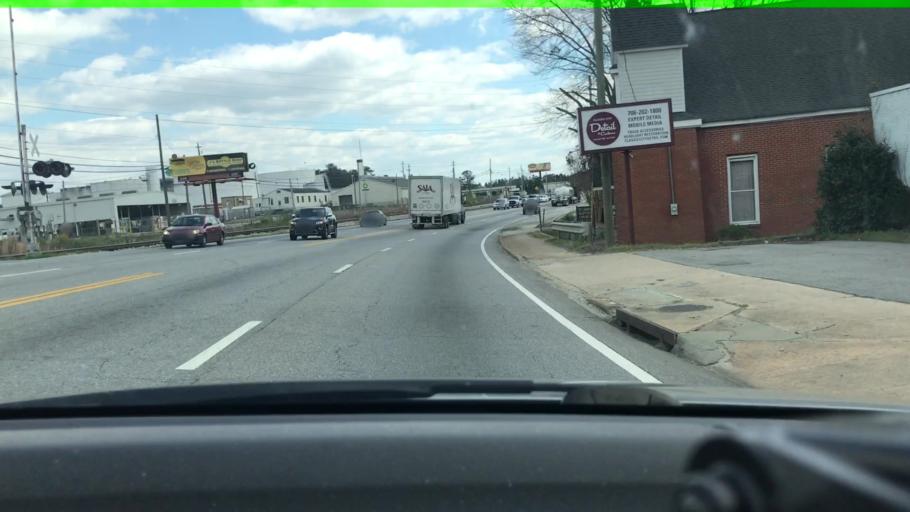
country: US
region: Georgia
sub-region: Clarke County
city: Country Club Estates
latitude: 33.9882
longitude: -83.4228
